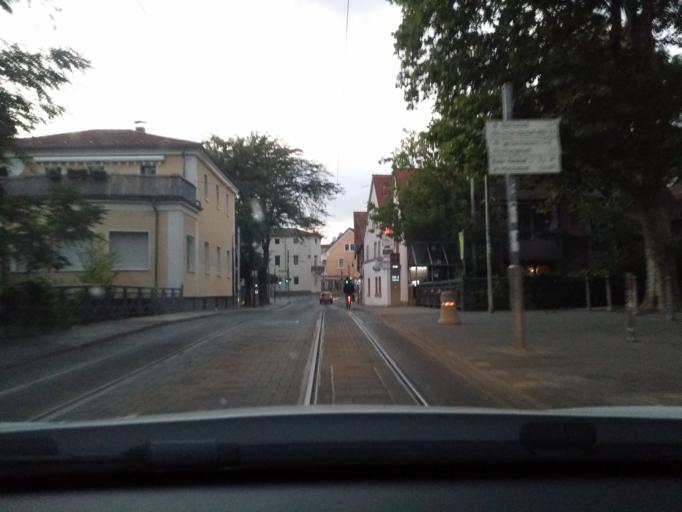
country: DE
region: Hesse
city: Pfungstadt
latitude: 49.8166
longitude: 8.6443
